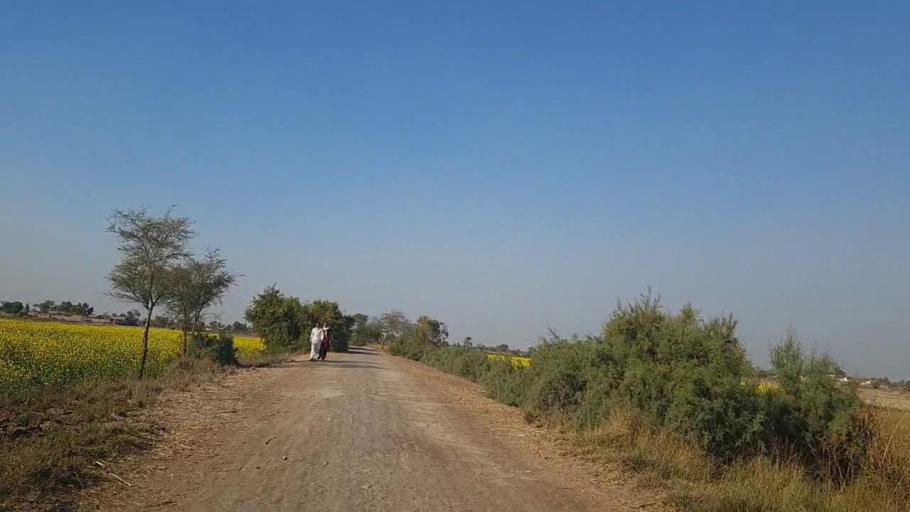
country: PK
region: Sindh
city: Daur
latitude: 26.3220
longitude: 68.1788
